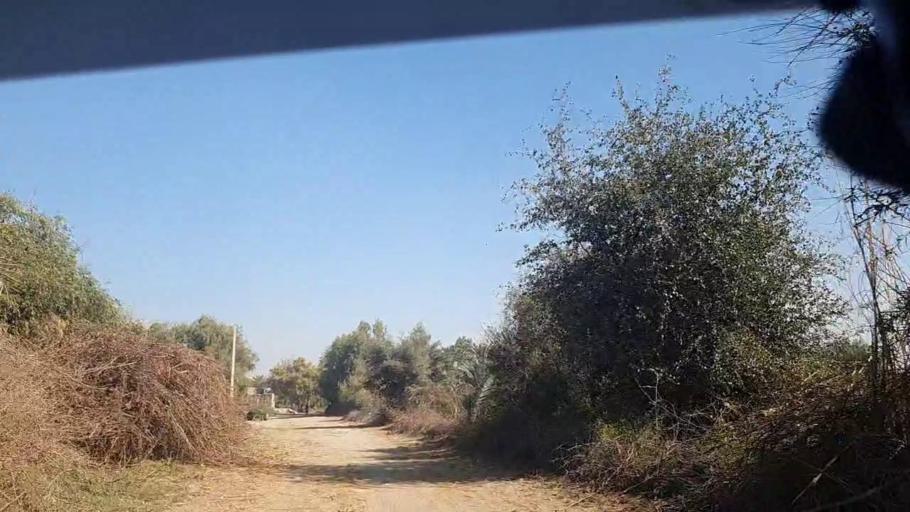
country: PK
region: Sindh
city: Khanpur
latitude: 27.6602
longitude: 69.2782
